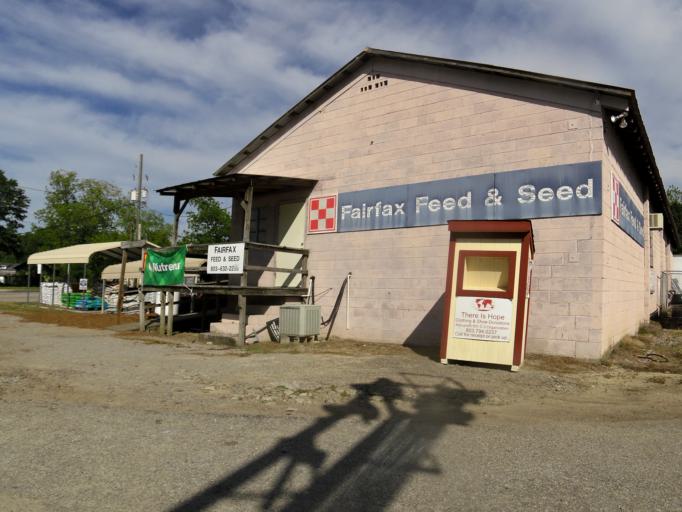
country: US
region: South Carolina
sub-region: Allendale County
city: Fairfax
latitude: 32.9613
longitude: -81.2401
